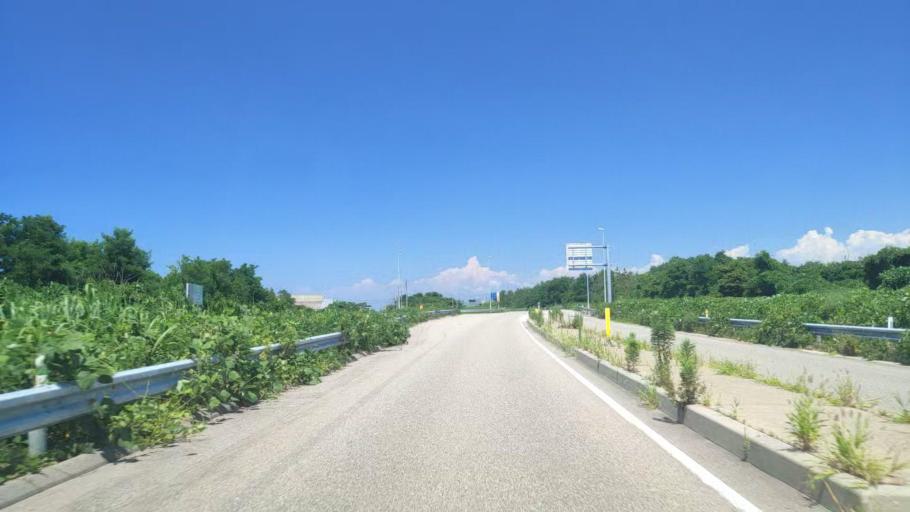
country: JP
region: Ishikawa
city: Kanazawa-shi
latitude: 36.6323
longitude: 136.6163
